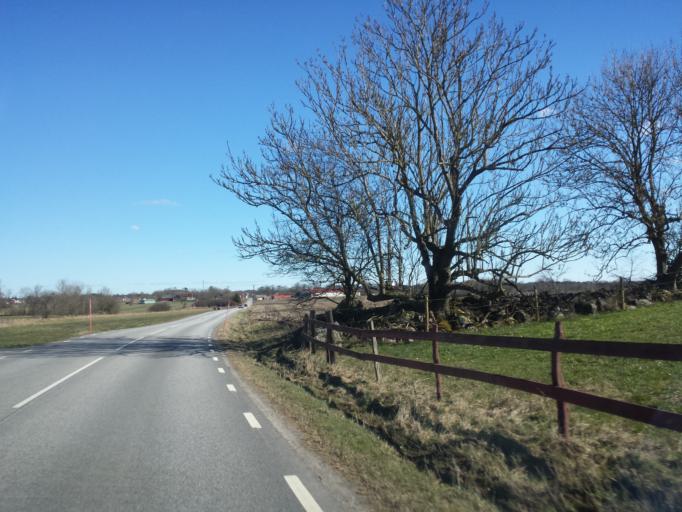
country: SE
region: Skane
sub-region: Tomelilla Kommun
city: Tomelilla
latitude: 55.6397
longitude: 13.8812
